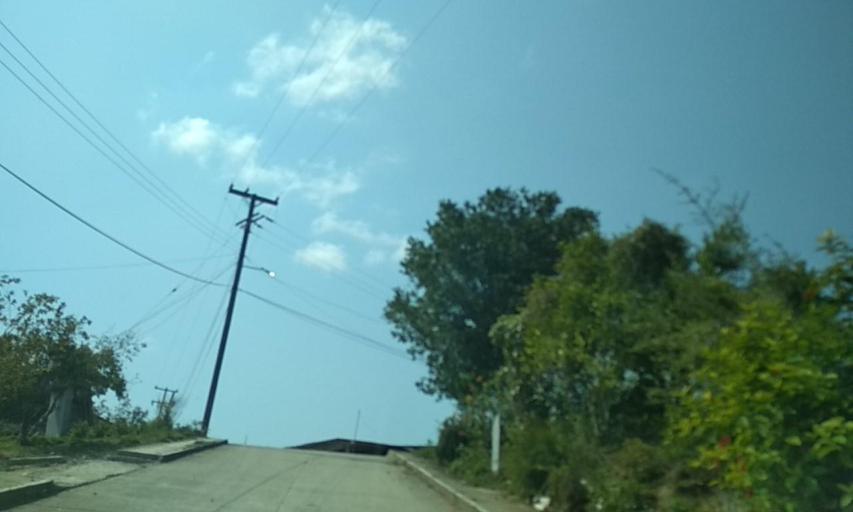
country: MX
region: Veracruz
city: Gutierrez Zamora
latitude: 20.3627
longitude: -97.1669
